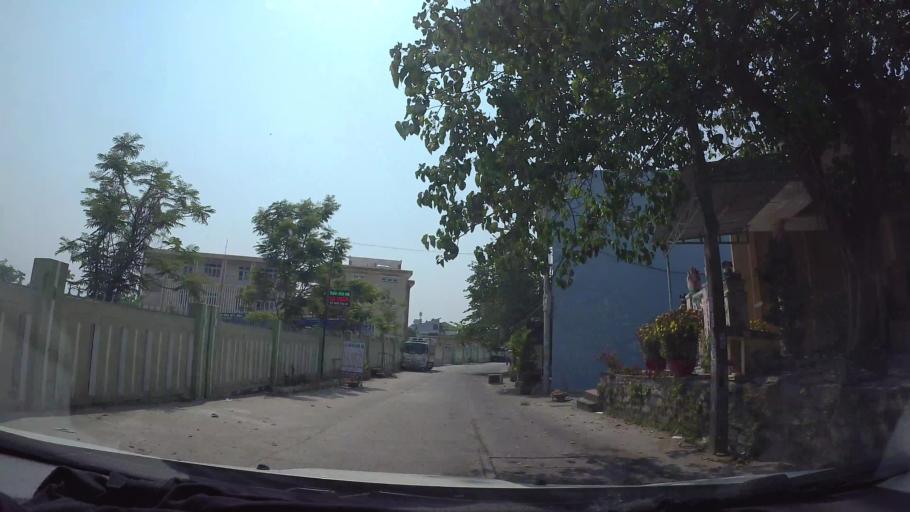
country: VN
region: Da Nang
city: Cam Le
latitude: 16.0110
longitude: 108.2053
